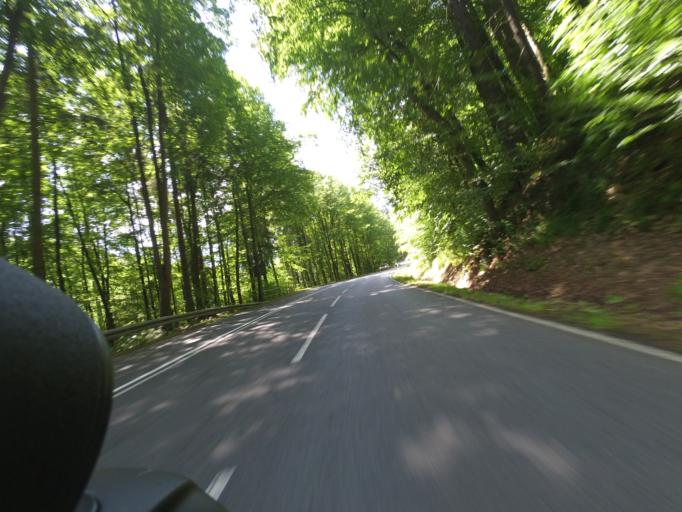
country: DE
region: Saxony
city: Hohnstein
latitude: 50.9840
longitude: 14.1041
